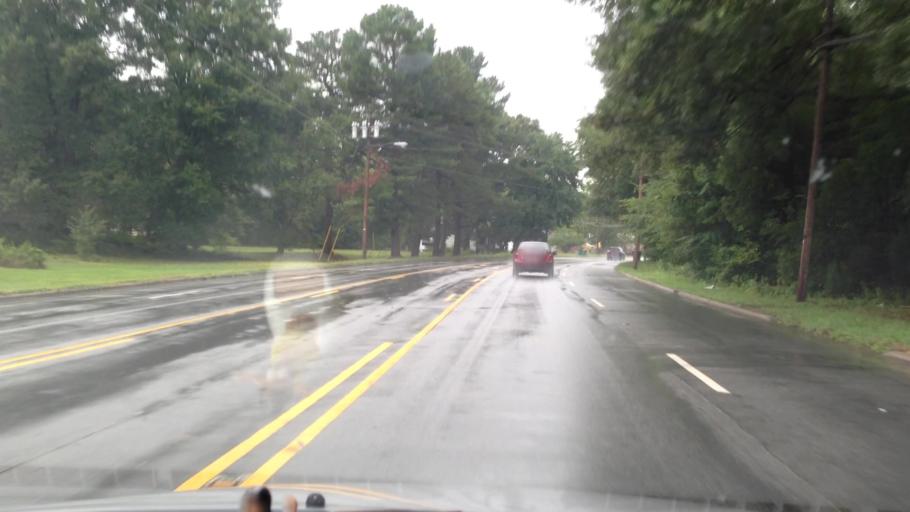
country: US
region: North Carolina
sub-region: Rockingham County
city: Mayodan
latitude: 36.3979
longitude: -79.9704
